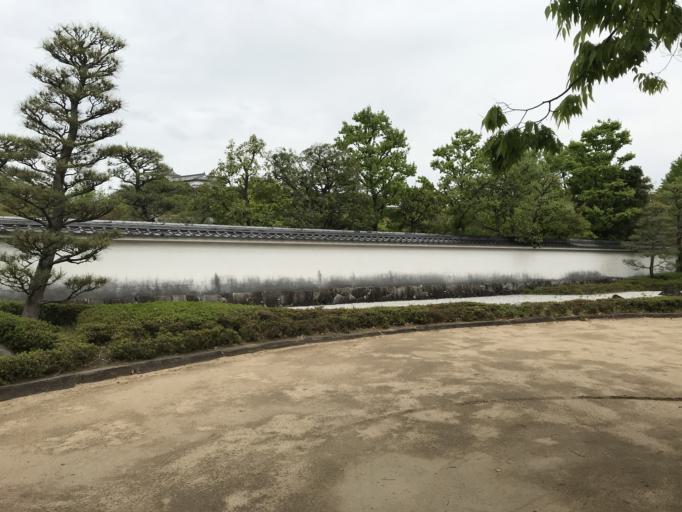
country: JP
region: Hyogo
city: Himeji
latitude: 34.8379
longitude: 134.6886
